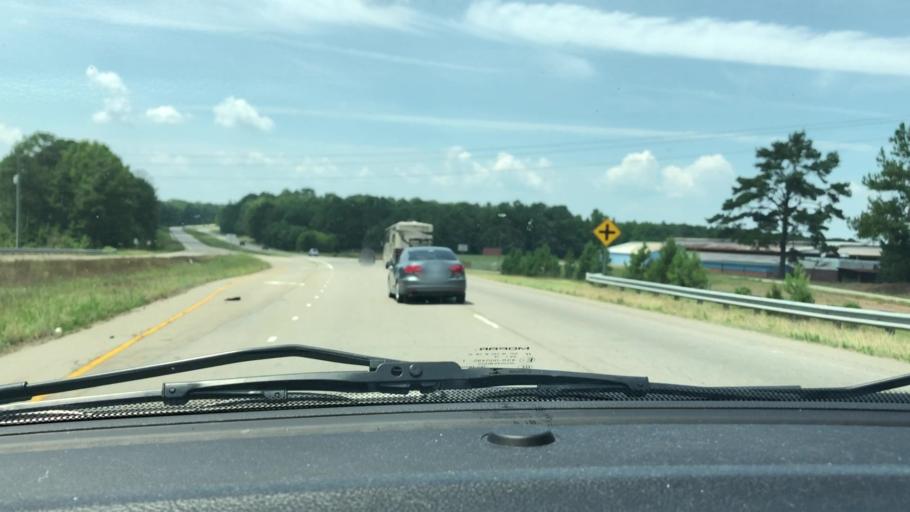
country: US
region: North Carolina
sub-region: Chatham County
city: Farmville
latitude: 35.5672
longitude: -79.2994
